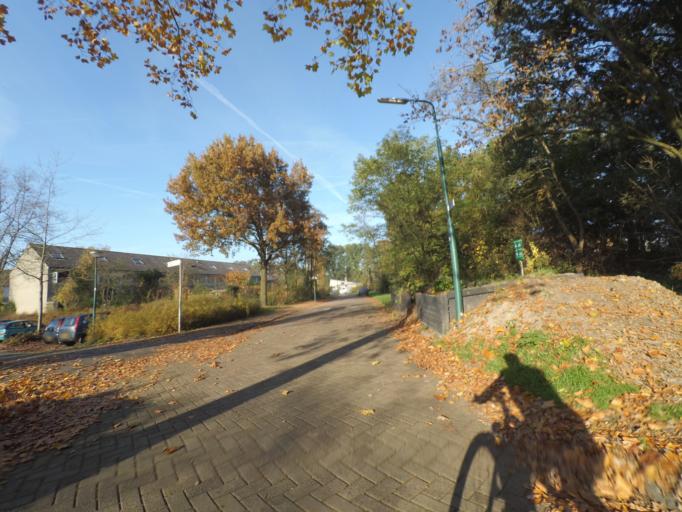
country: NL
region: Utrecht
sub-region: Gemeente Leusden
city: Leusden
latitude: 52.1377
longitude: 5.4467
